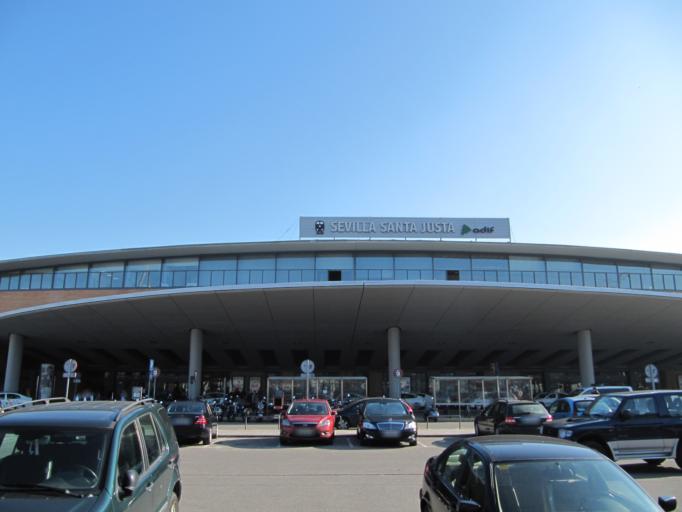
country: ES
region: Andalusia
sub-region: Provincia de Sevilla
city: Sevilla
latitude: 37.3915
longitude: -5.9760
